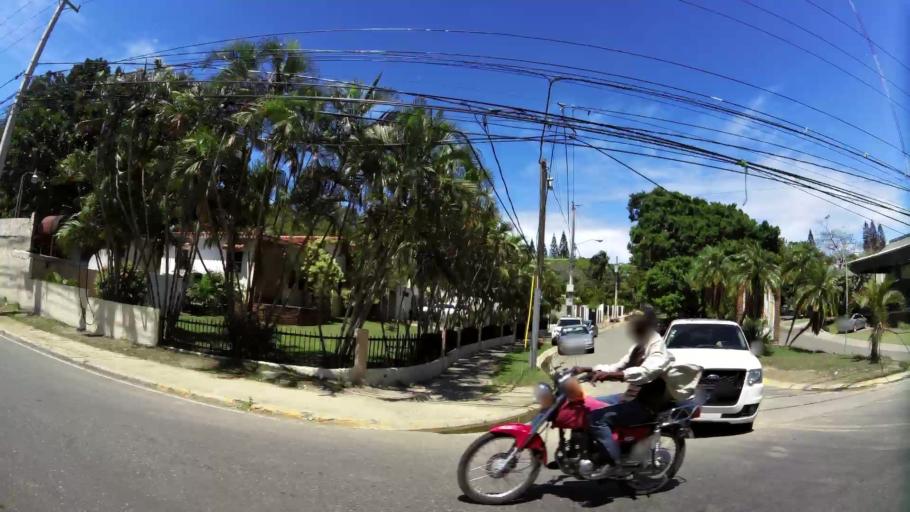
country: DO
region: Santiago
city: Santiago de los Caballeros
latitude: 19.4531
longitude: -70.6922
